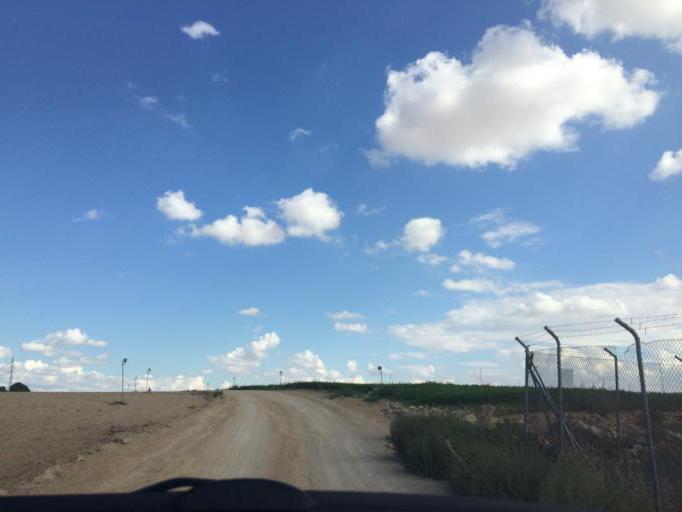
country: ES
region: Castille-La Mancha
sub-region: Provincia de Albacete
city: Albacete
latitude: 38.9587
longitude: -1.8741
